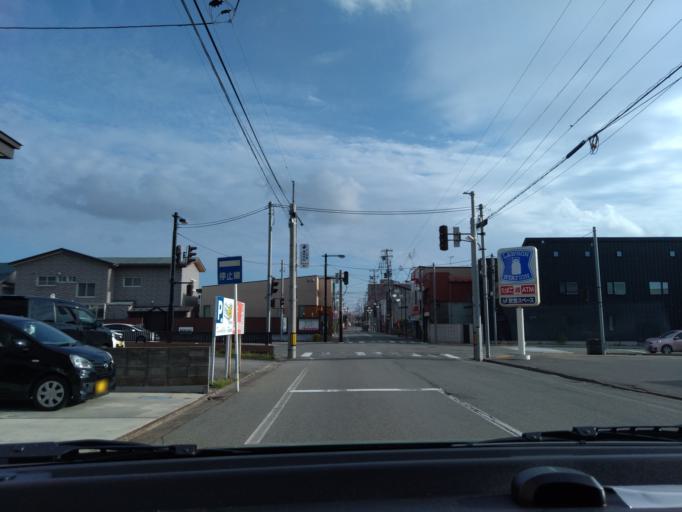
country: JP
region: Akita
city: Akita Shi
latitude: 39.7577
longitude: 140.0693
